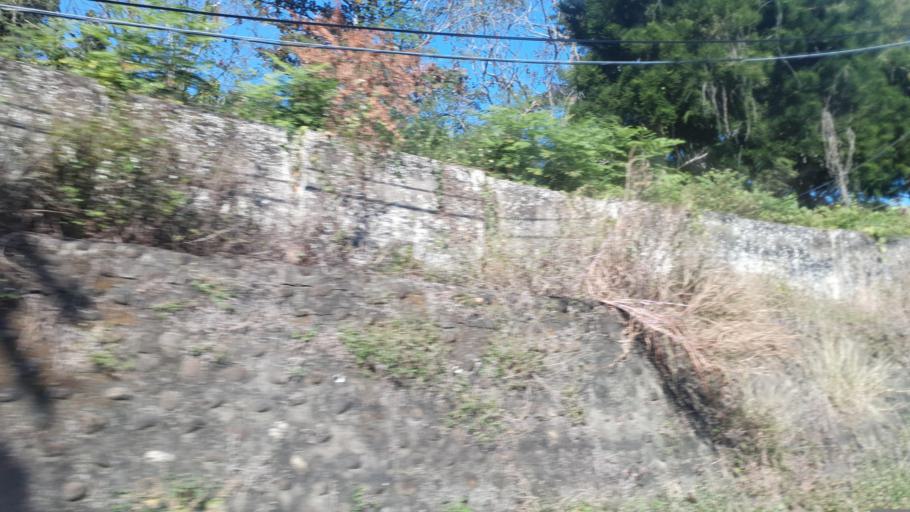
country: TW
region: Taiwan
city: Yujing
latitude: 23.0427
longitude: 120.3626
